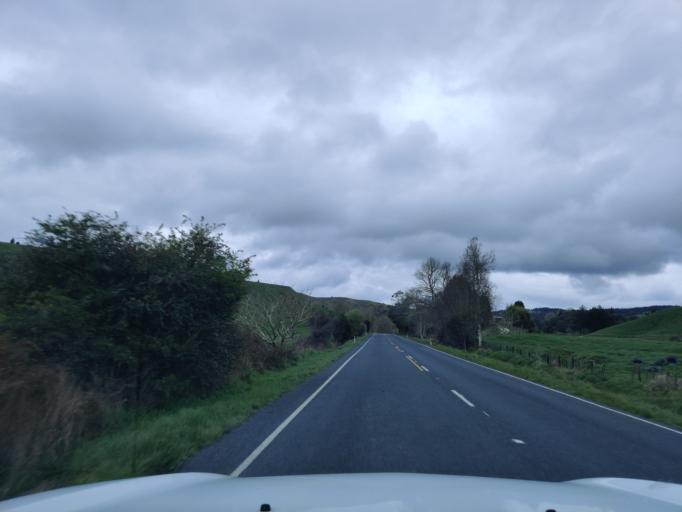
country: NZ
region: Waikato
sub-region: Otorohanga District
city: Otorohanga
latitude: -38.5206
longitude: 175.1854
